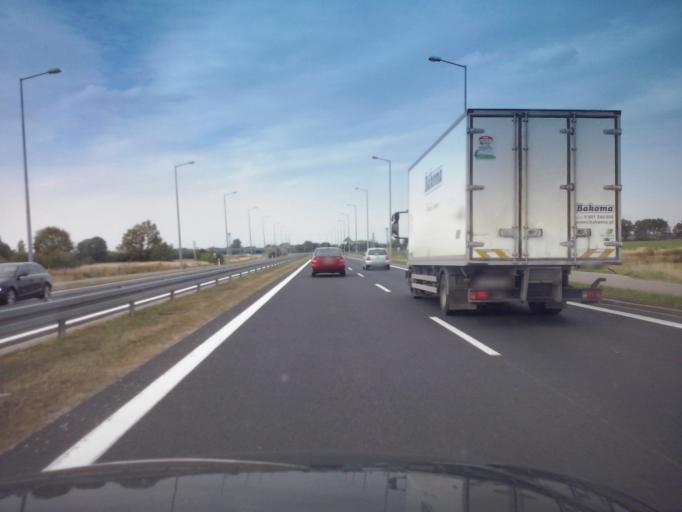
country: PL
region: Subcarpathian Voivodeship
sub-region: Powiat stalowowolski
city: Stalowa Wola
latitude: 50.6027
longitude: 22.0434
